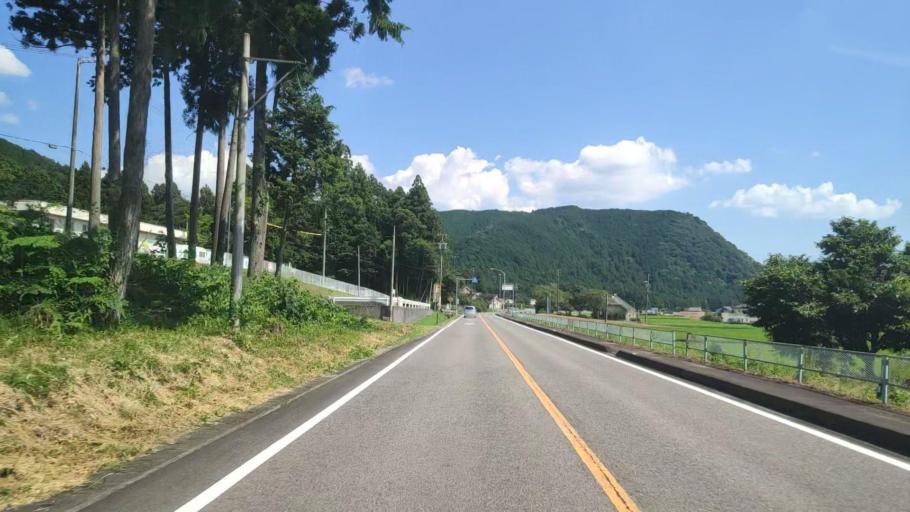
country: JP
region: Gifu
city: Godo
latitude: 35.5377
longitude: 136.6487
